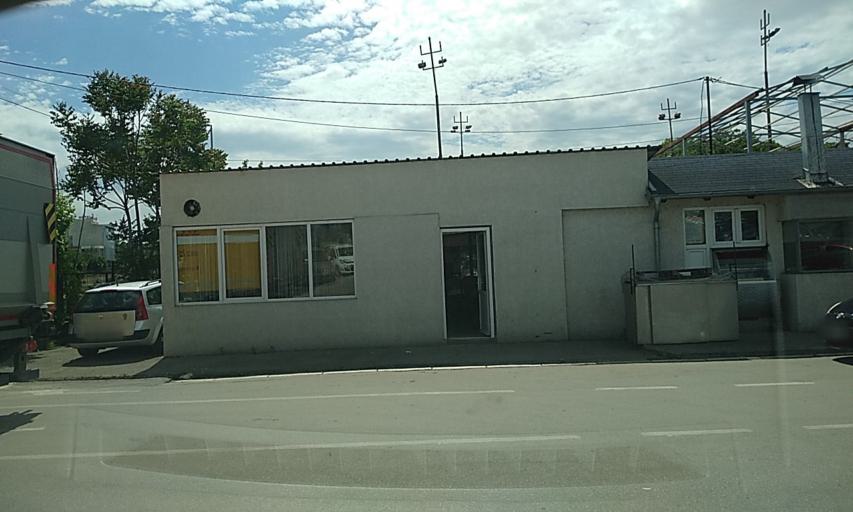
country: RS
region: Central Serbia
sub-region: Nisavski Okrug
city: Nis
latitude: 43.3269
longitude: 21.9016
